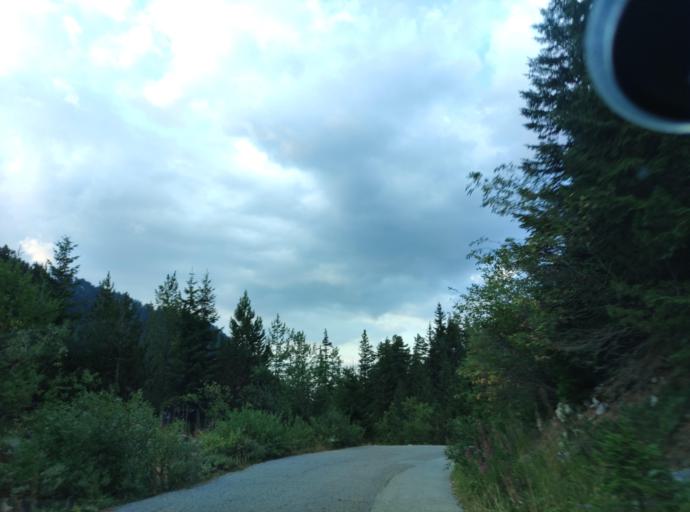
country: BG
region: Blagoevgrad
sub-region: Obshtina Bansko
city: Bansko
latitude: 41.7678
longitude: 23.4276
